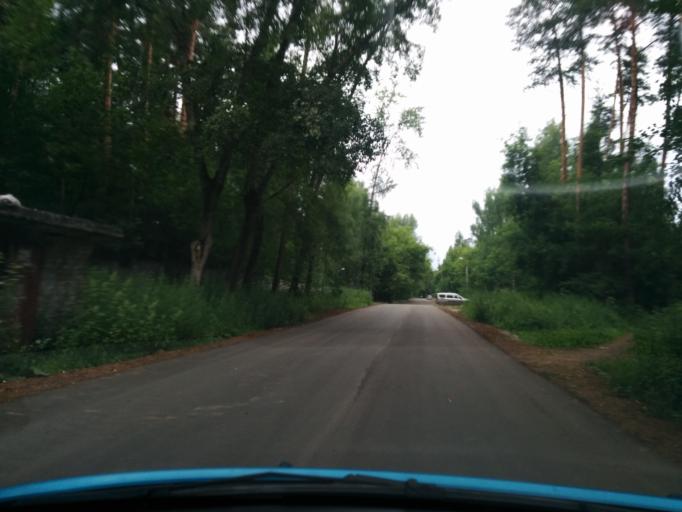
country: RU
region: Perm
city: Kondratovo
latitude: 58.0228
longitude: 56.0100
